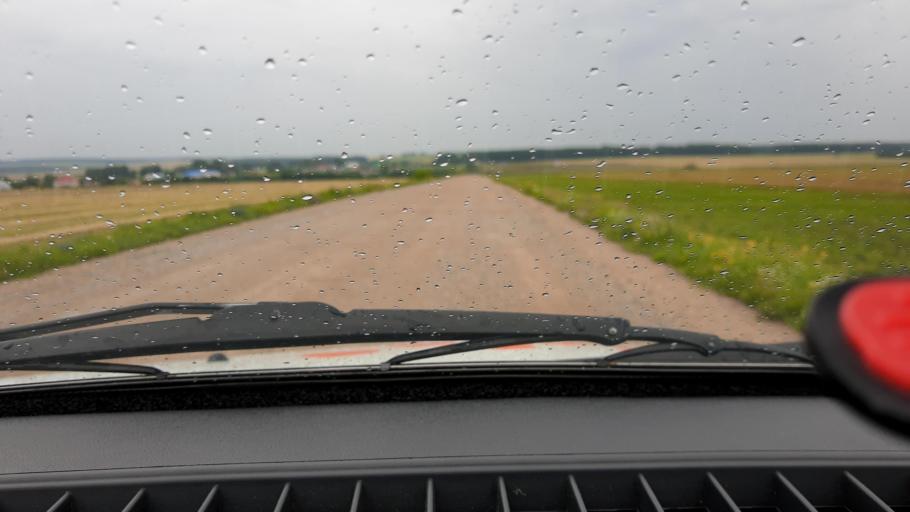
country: RU
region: Bashkortostan
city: Karmaskaly
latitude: 54.3873
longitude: 56.1244
